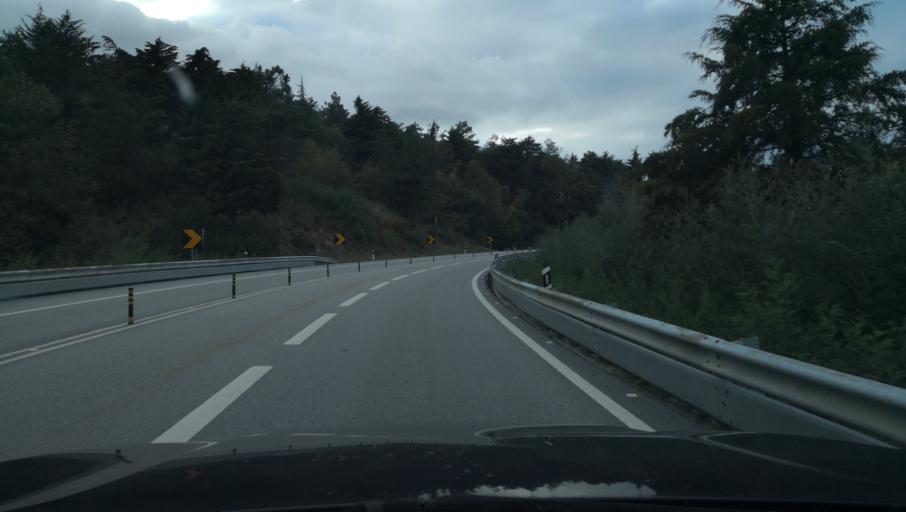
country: PT
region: Vila Real
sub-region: Santa Marta de Penaguiao
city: Santa Marta de Penaguiao
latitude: 41.2813
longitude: -7.8793
